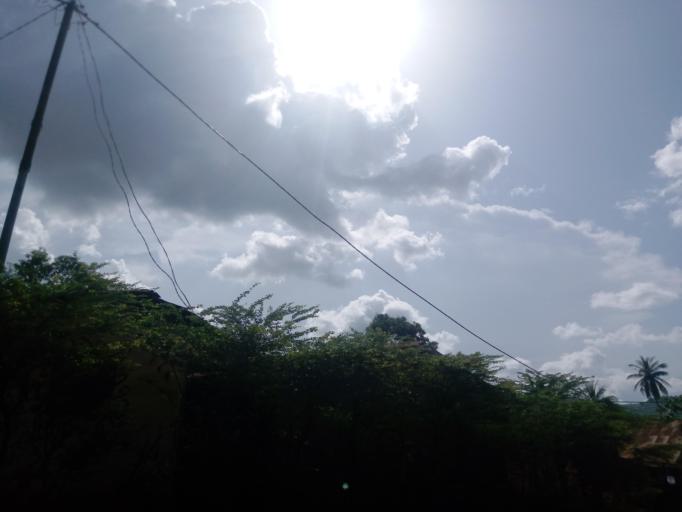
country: SL
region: Northern Province
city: Makeni
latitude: 8.9042
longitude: -12.0333
